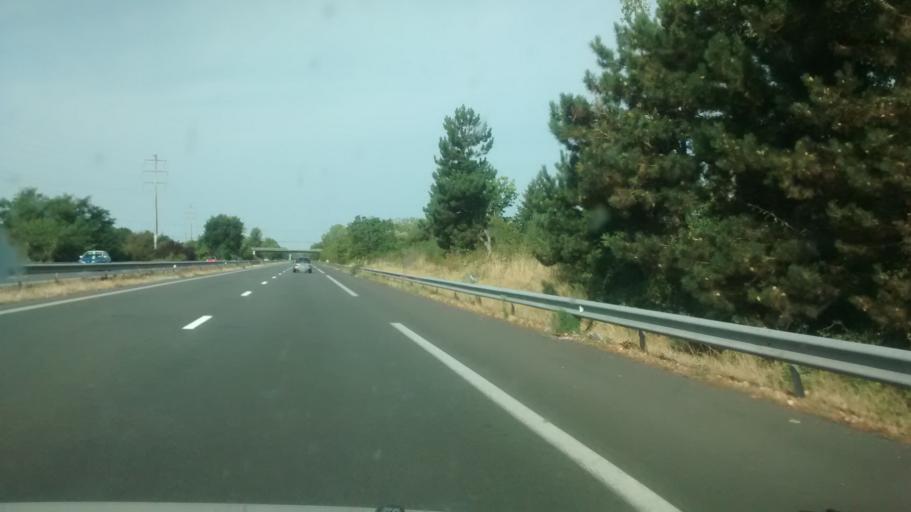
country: FR
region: Aquitaine
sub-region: Departement du Lot-et-Garonne
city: Sainte-Colombe-en-Bruilhois
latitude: 44.2118
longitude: 0.4620
